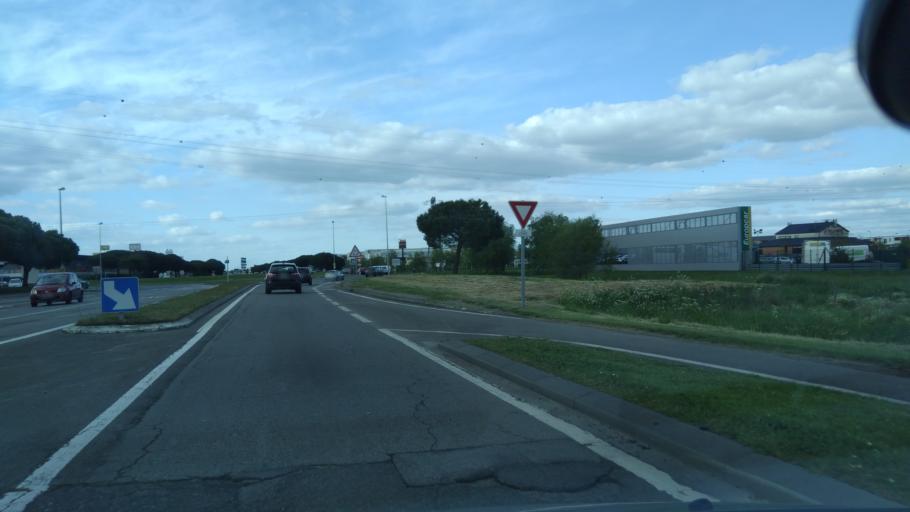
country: FR
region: Pays de la Loire
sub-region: Departement de la Loire-Atlantique
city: Saint-Nazaire
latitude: 47.2924
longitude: -2.2086
